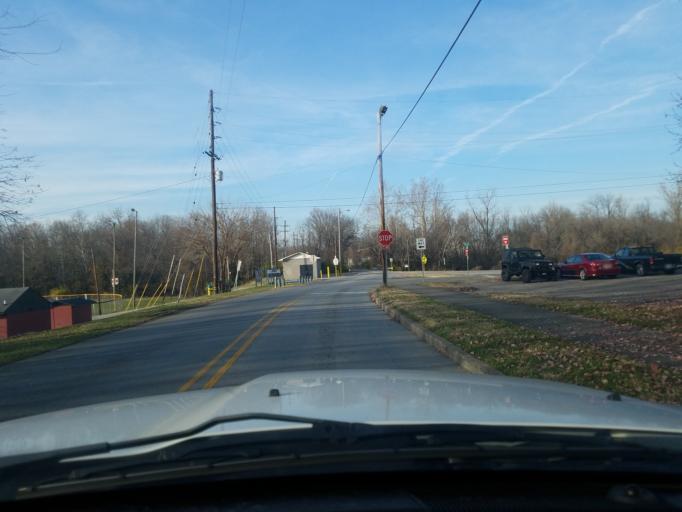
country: US
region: Indiana
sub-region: Floyd County
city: New Albany
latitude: 38.2868
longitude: -85.8271
